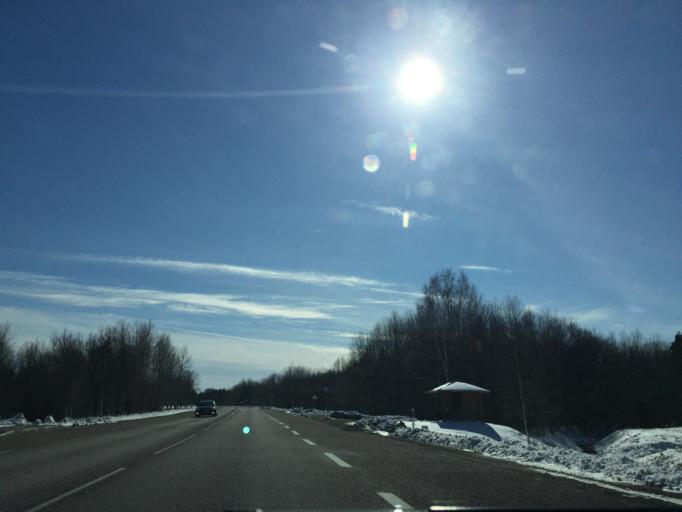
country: EE
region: Saare
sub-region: Kuressaare linn
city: Kuressaare
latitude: 58.3443
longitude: 22.6726
